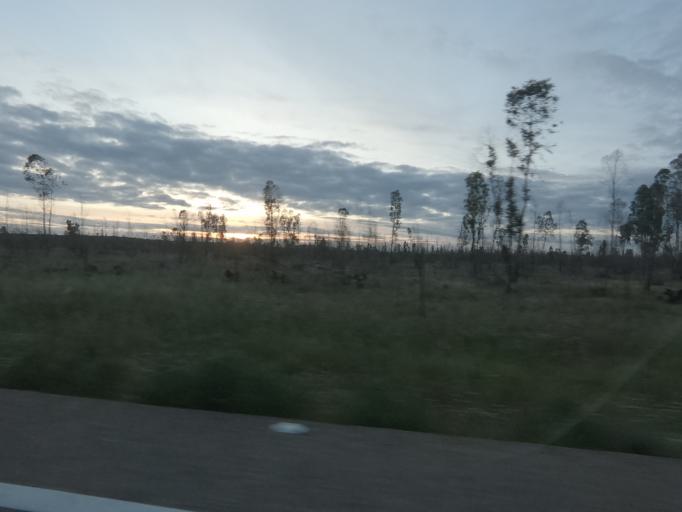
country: ES
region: Extremadura
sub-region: Provincia de Badajoz
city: Badajoz
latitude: 38.9830
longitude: -6.8820
